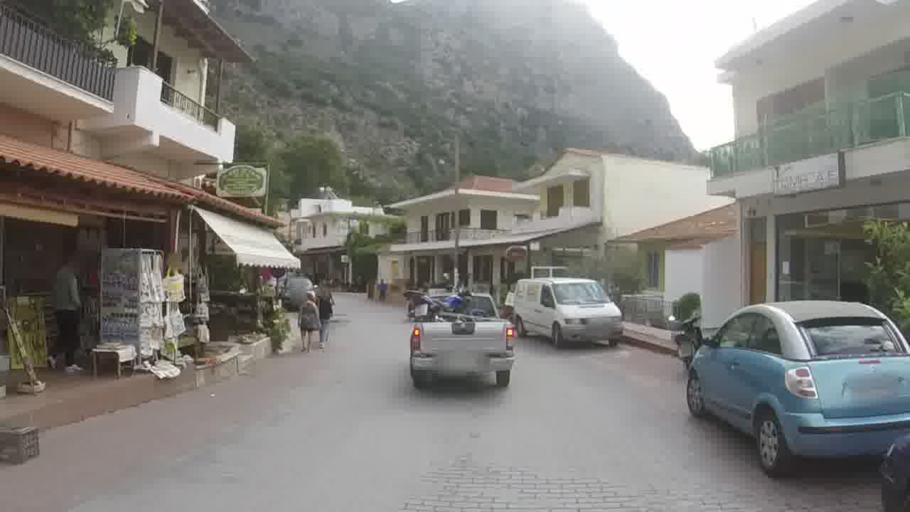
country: GR
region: Crete
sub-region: Nomos Rethymnis
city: Agia Foteini
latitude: 35.2182
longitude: 24.5351
